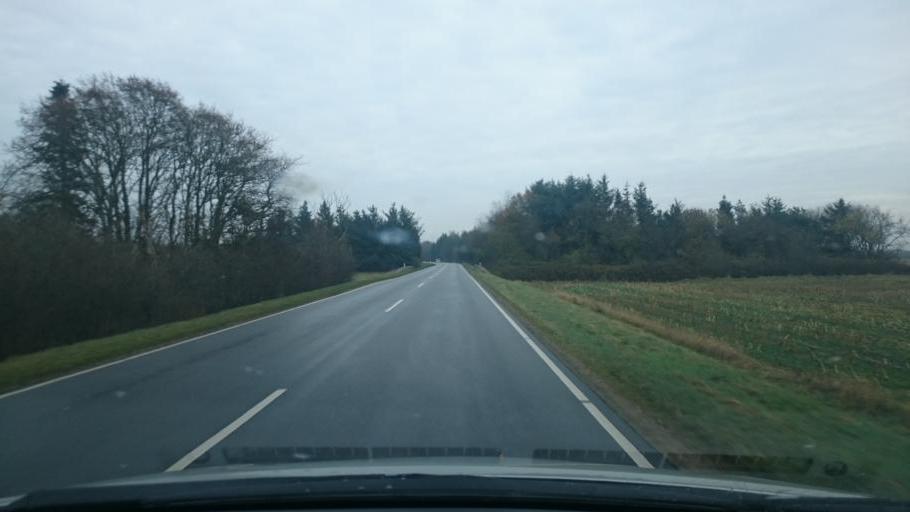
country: DK
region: South Denmark
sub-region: Esbjerg Kommune
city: Ribe
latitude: 55.3337
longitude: 8.8554
